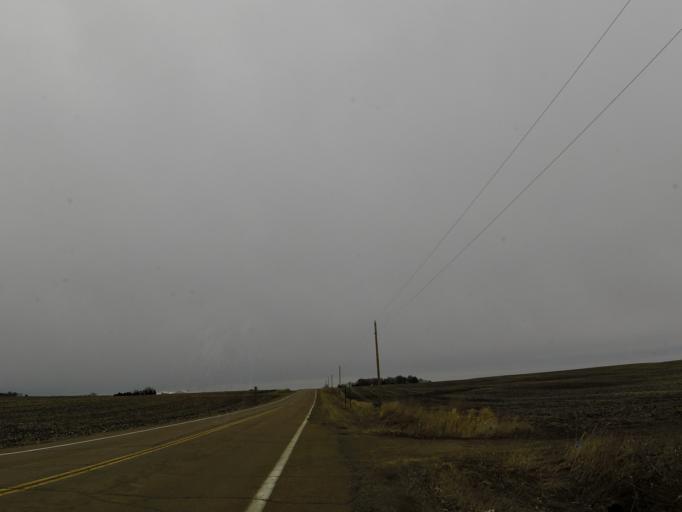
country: US
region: Minnesota
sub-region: Scott County
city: Belle Plaine
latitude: 44.5446
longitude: -93.7986
